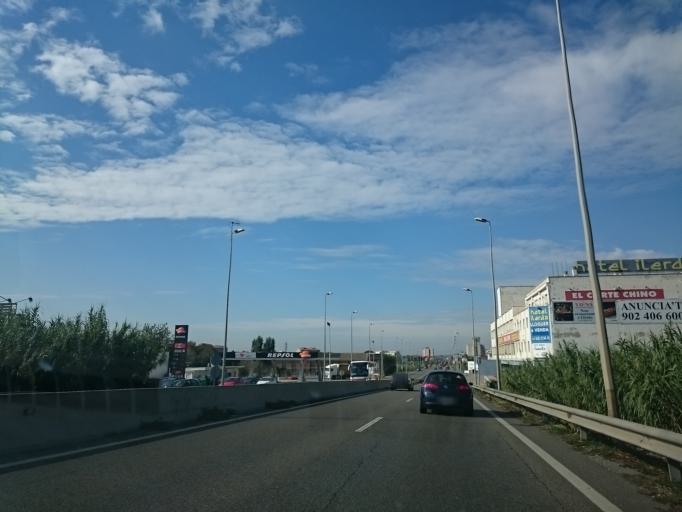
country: ES
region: Catalonia
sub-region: Provincia de Lleida
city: Lleida
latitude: 41.6120
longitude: 0.6447
